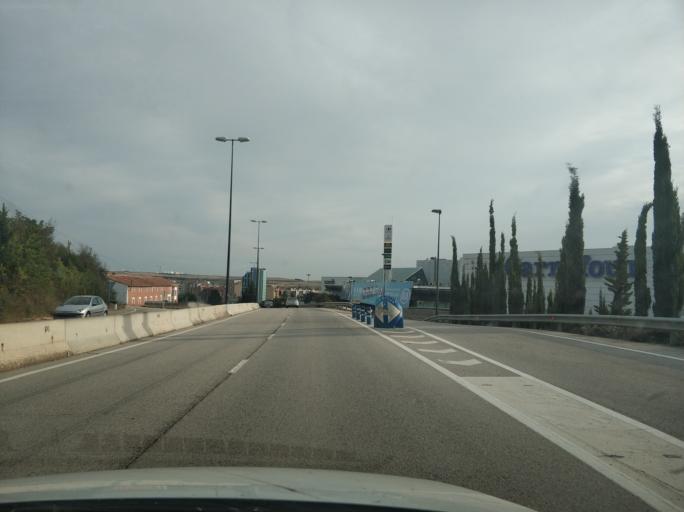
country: ES
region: Castille and Leon
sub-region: Provincia de Burgos
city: Burgos
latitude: 42.3612
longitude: -3.6944
